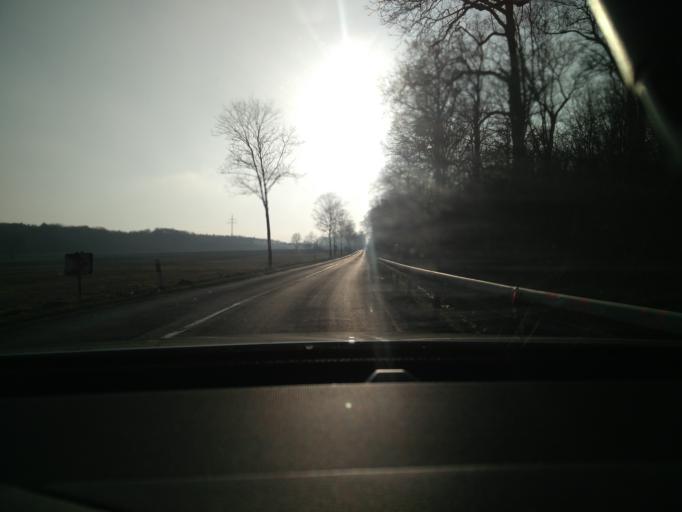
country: DE
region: Lower Saxony
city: Laatzen
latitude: 52.3161
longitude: 9.8586
